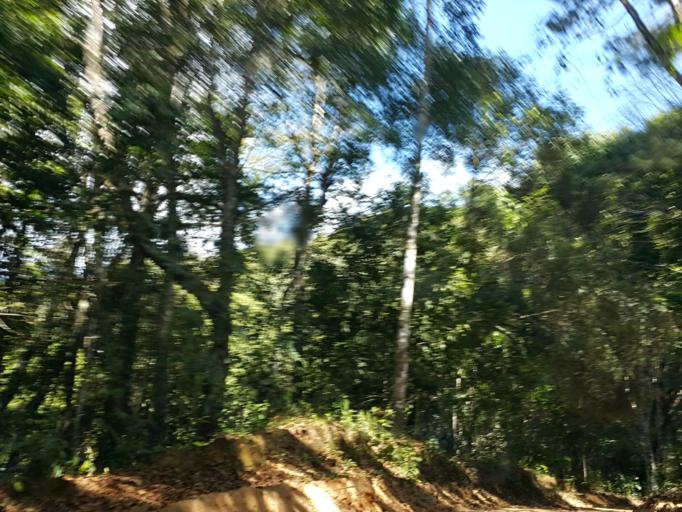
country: TH
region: Chiang Mai
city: Wiang Haeng
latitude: 19.5292
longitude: 98.8101
